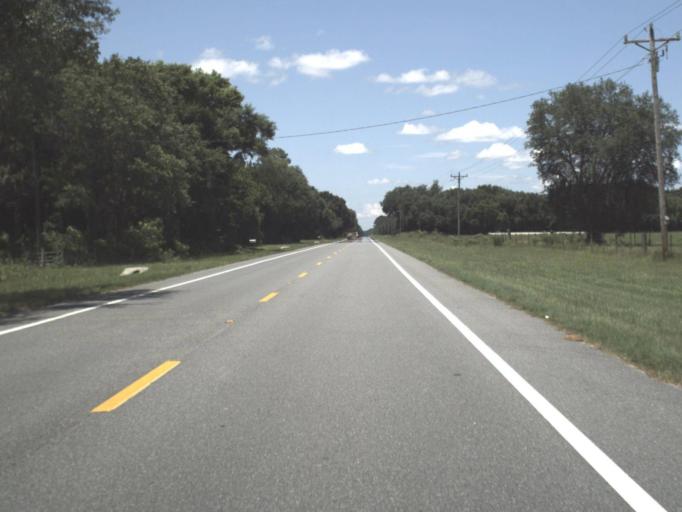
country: US
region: Florida
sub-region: Lafayette County
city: Mayo
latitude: 29.8926
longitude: -82.9544
